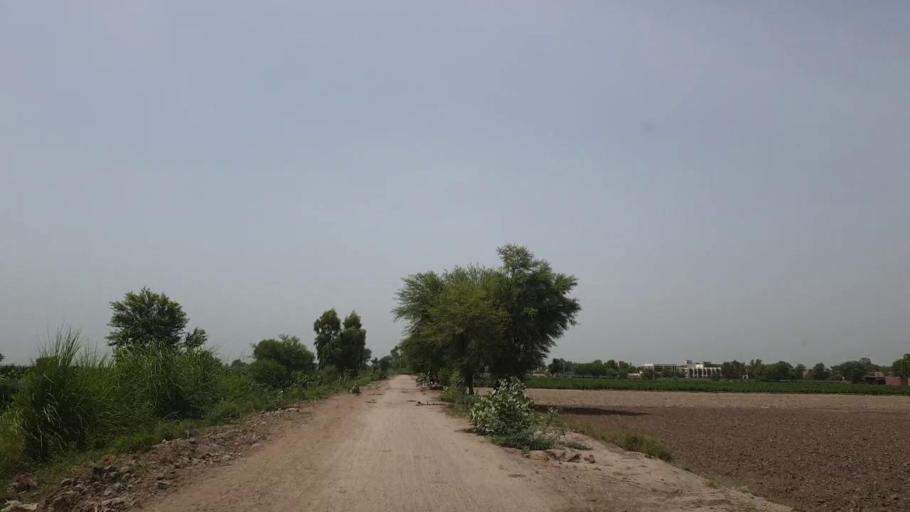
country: PK
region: Sindh
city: Sakrand
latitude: 26.1305
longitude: 68.2865
